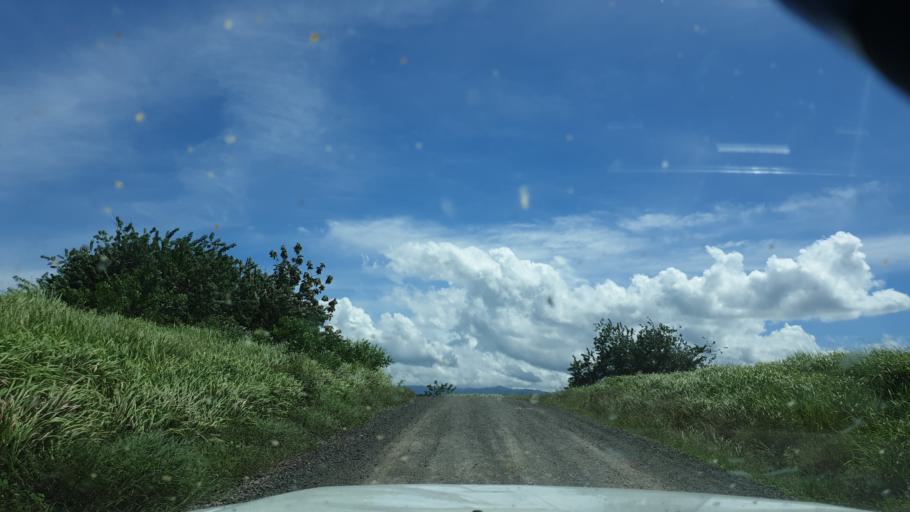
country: PG
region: Madang
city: Madang
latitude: -4.6226
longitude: 145.5601
